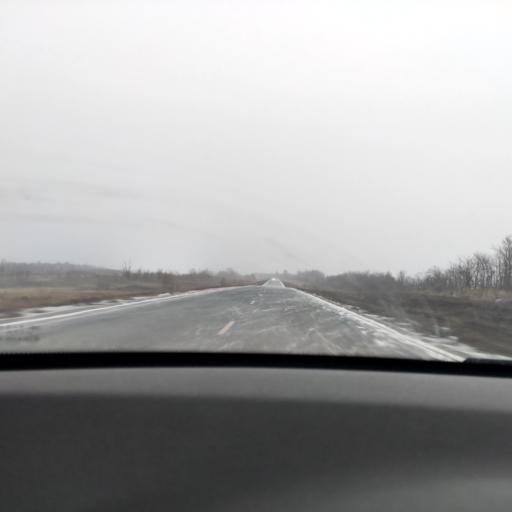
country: RU
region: Samara
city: Novokuybyshevsk
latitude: 52.9158
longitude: 49.9270
